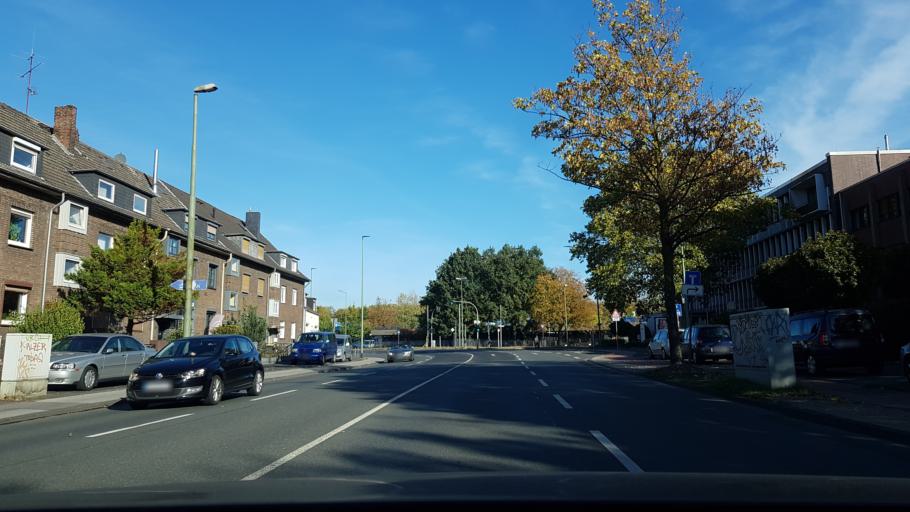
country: DE
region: North Rhine-Westphalia
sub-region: Regierungsbezirk Dusseldorf
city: Duisburg
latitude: 51.4446
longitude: 6.7945
